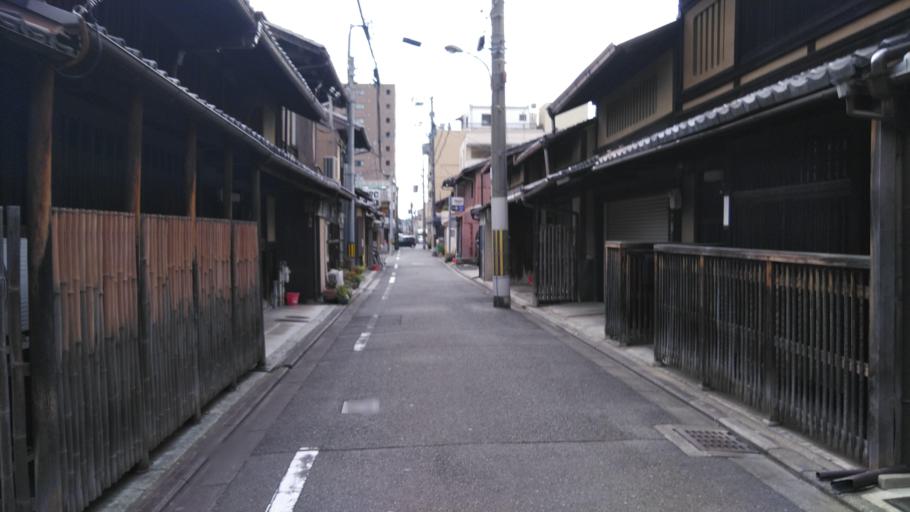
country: JP
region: Kyoto
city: Kyoto
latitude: 34.9973
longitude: 135.7484
